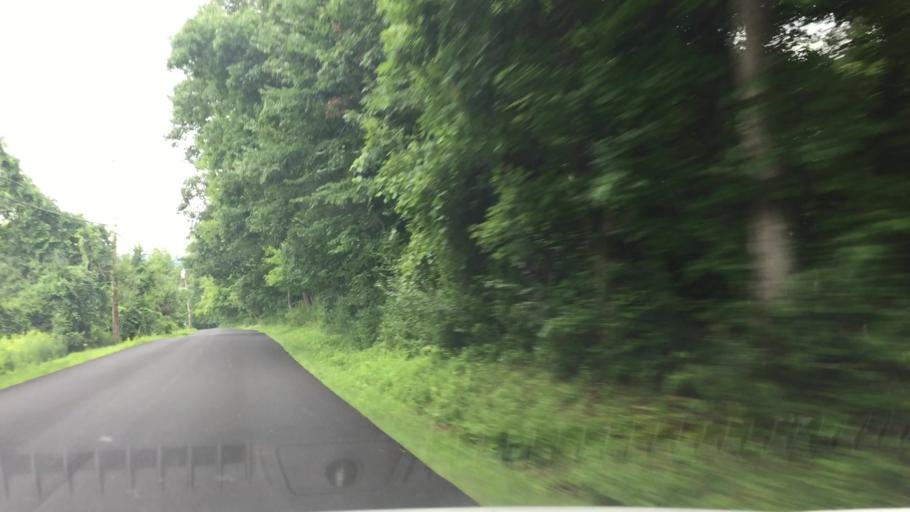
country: US
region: Massachusetts
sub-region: Berkshire County
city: Housatonic
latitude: 42.2489
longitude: -73.4063
